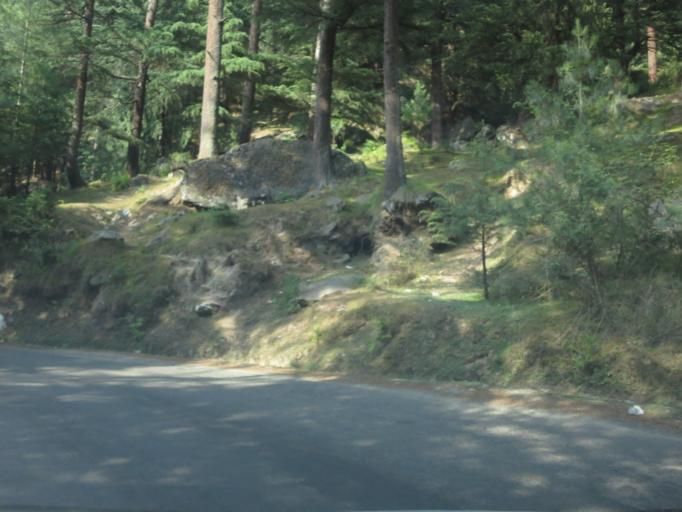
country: IN
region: Himachal Pradesh
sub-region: Kulu
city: Nagar
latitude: 32.1651
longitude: 77.1931
